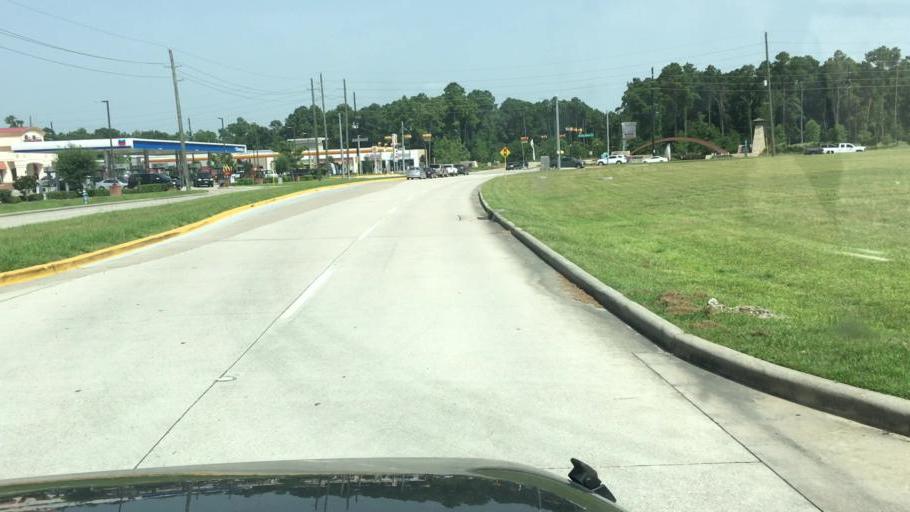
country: US
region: Texas
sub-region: Harris County
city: Atascocita
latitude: 29.9809
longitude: -95.1663
